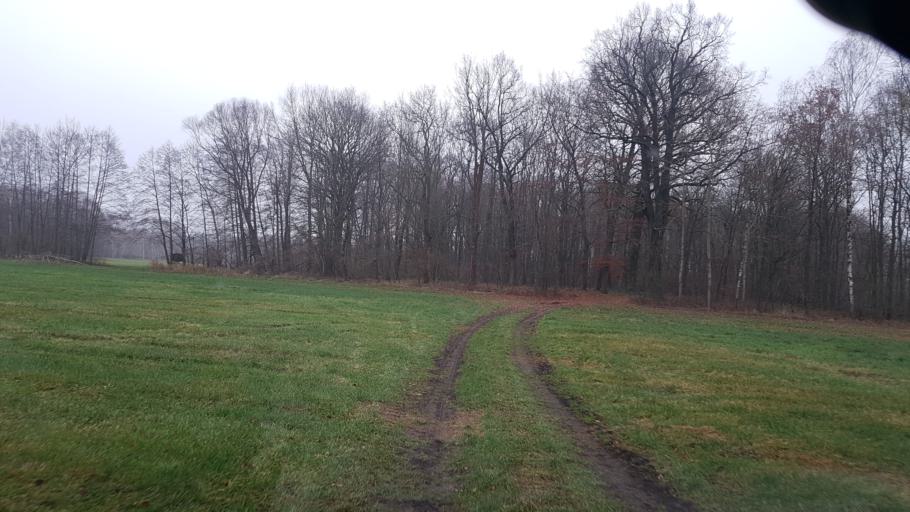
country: DE
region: Brandenburg
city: Altdobern
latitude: 51.6743
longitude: 13.9994
